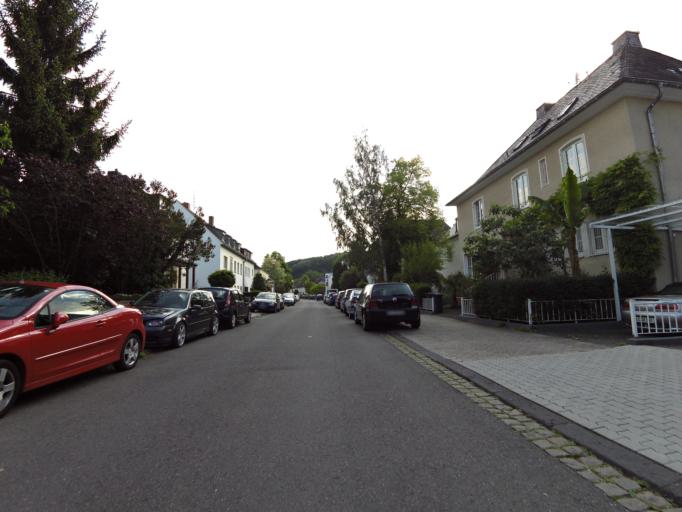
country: DE
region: Rheinland-Pfalz
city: Koblenz
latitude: 50.3410
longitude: 7.5905
